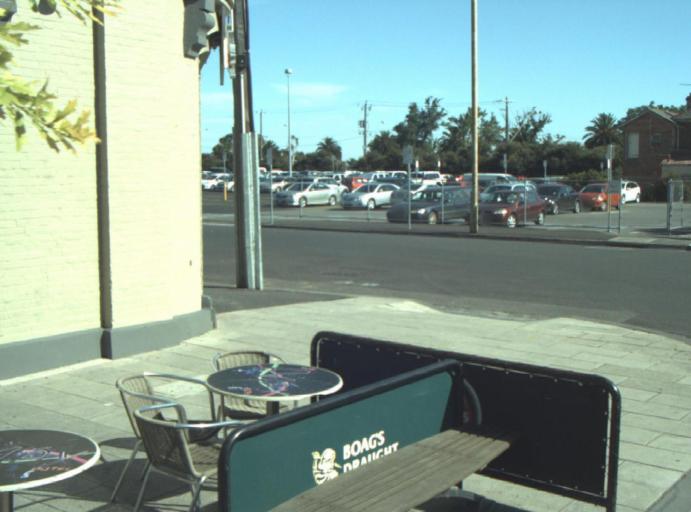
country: AU
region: Victoria
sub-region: Greater Geelong
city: Geelong
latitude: -38.1436
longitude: 144.3595
